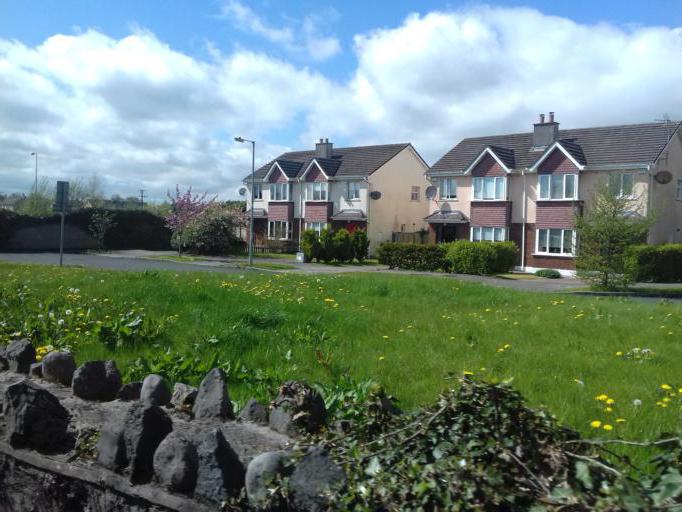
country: IE
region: Leinster
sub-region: Laois
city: Portlaoise
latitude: 53.0403
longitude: -7.3025
